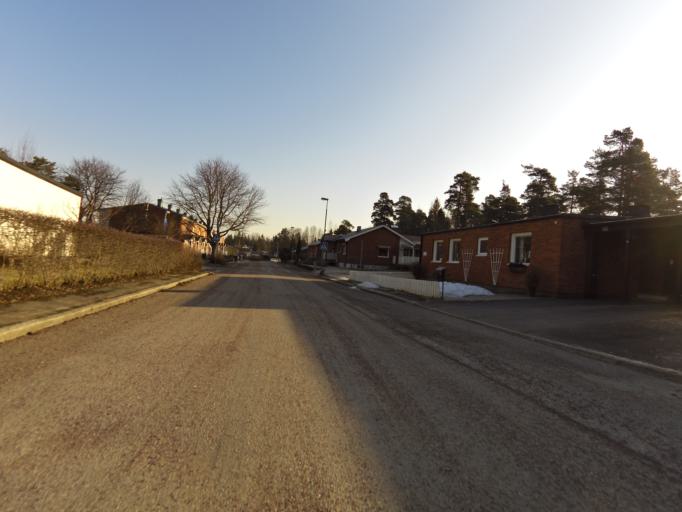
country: SE
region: Gaevleborg
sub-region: Gavle Kommun
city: Gavle
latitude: 60.6588
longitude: 17.1196
